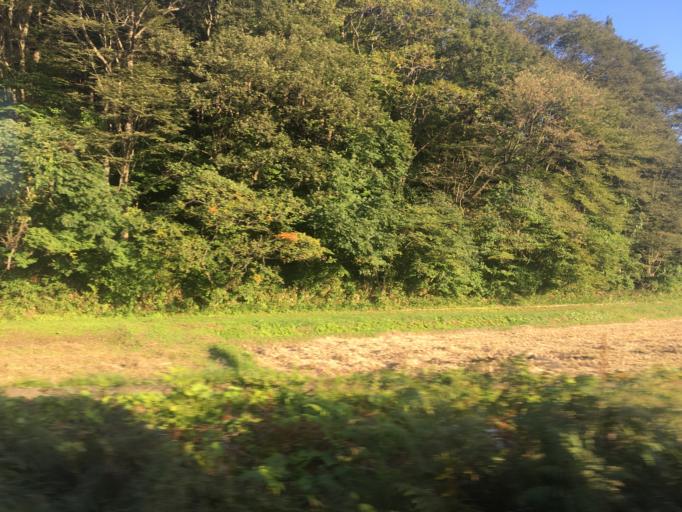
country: JP
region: Akita
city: Takanosu
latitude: 40.2059
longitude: 140.3515
